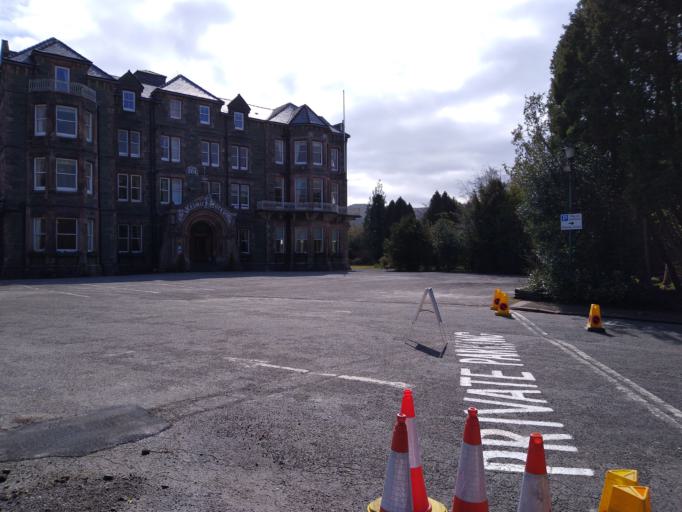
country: GB
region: England
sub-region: Cumbria
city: Keswick
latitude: 54.6037
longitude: -3.1310
